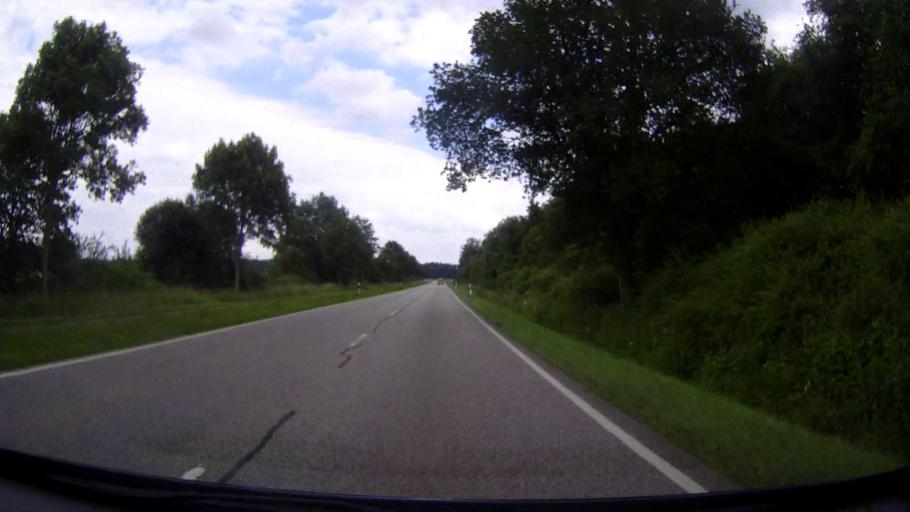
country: DE
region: Schleswig-Holstein
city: Tappendorf
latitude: 54.0833
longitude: 9.6920
